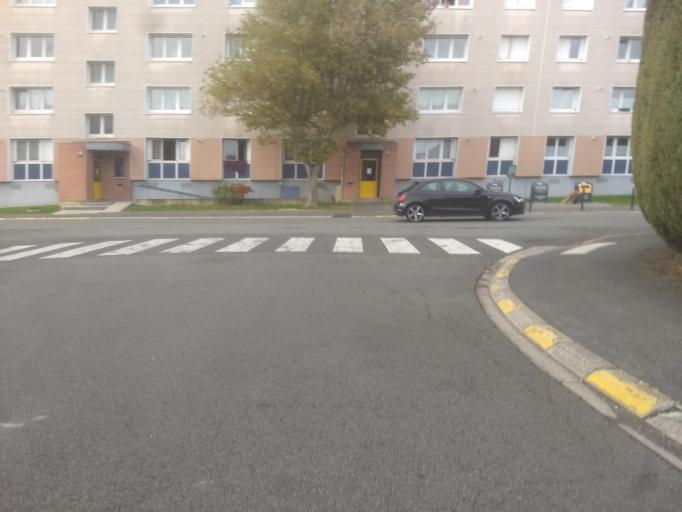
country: FR
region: Nord-Pas-de-Calais
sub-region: Departement du Pas-de-Calais
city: Achicourt
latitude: 50.2698
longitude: 2.7676
